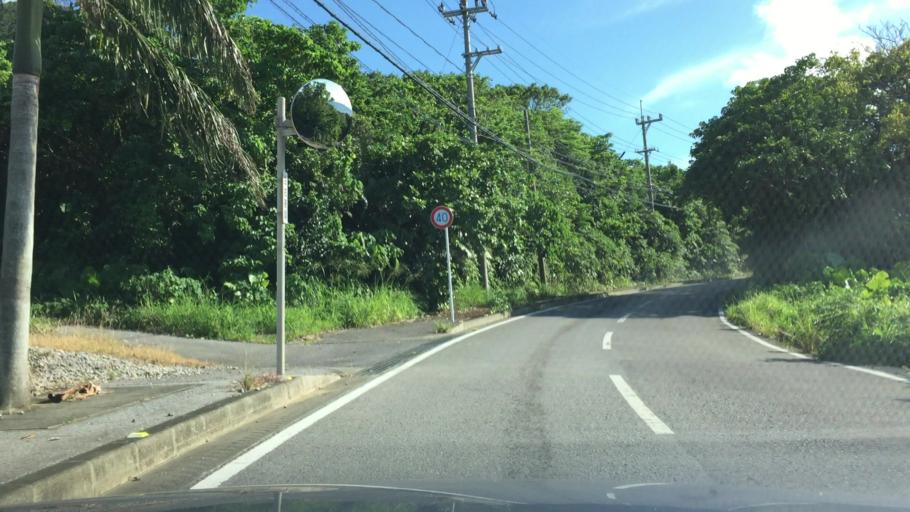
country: JP
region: Okinawa
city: Ishigaki
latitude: 24.4517
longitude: 124.1859
